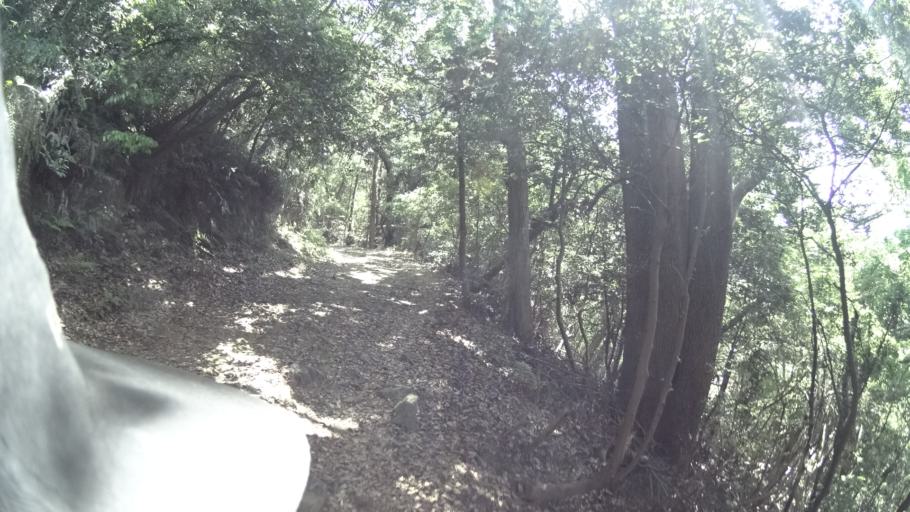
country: JP
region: Shizuoka
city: Kosai-shi
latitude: 34.7394
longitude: 137.4873
